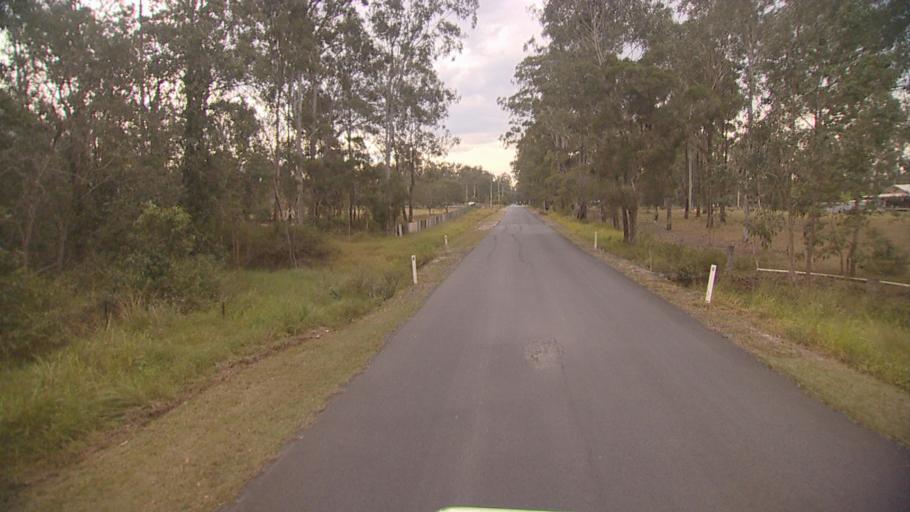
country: AU
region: Queensland
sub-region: Logan
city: Chambers Flat
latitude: -27.7729
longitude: 153.1157
